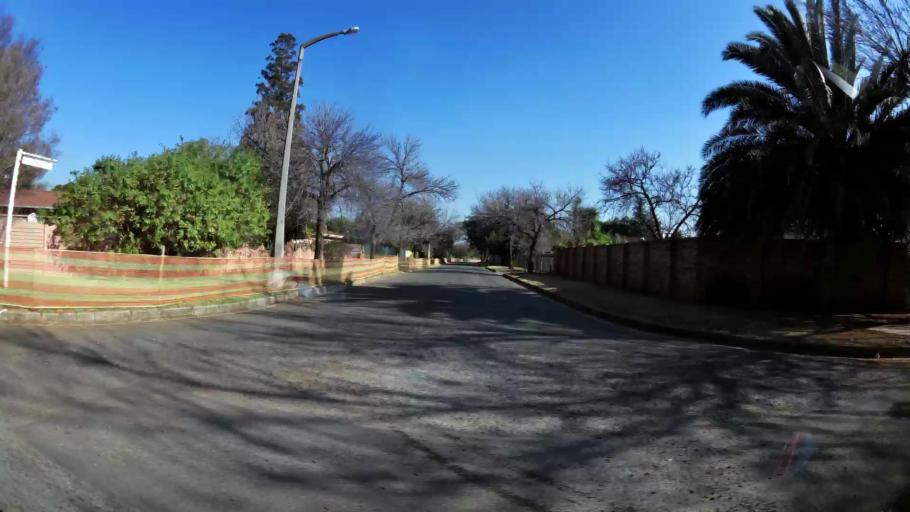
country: ZA
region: Gauteng
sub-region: Ekurhuleni Metropolitan Municipality
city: Benoni
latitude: -26.1513
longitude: 28.3077
